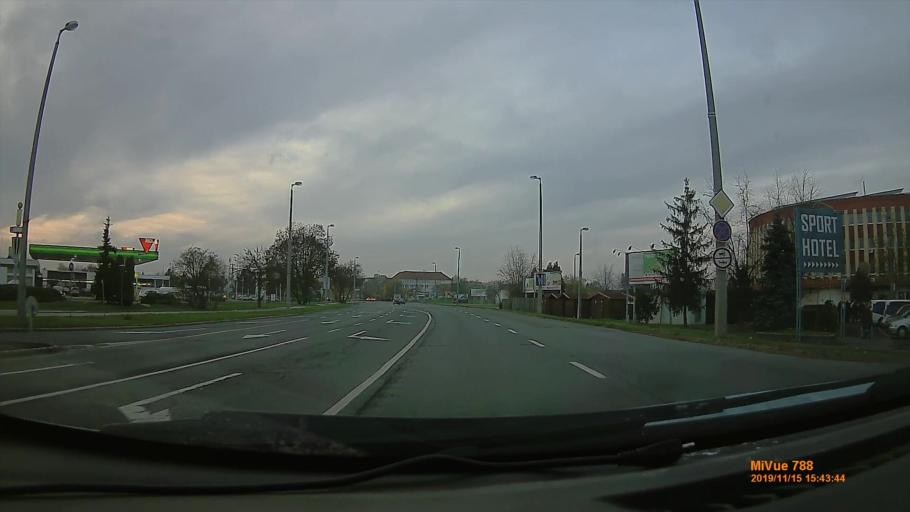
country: HU
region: Bekes
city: Bekescsaba
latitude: 46.6814
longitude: 21.1140
